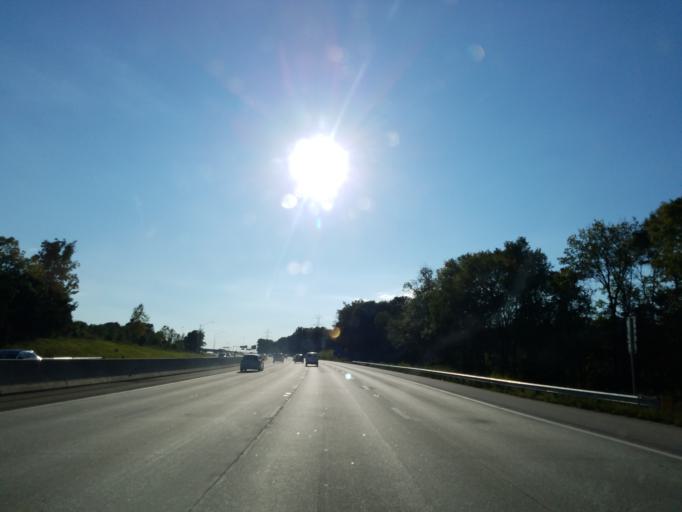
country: US
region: North Carolina
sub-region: Cabarrus County
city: Kannapolis
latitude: 35.4384
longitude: -80.6489
